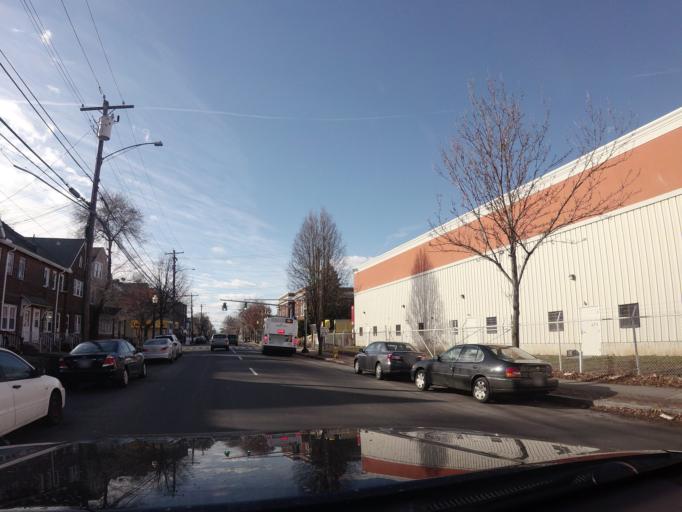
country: US
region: Connecticut
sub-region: Fairfield County
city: Stratford
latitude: 41.1824
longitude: -73.1601
